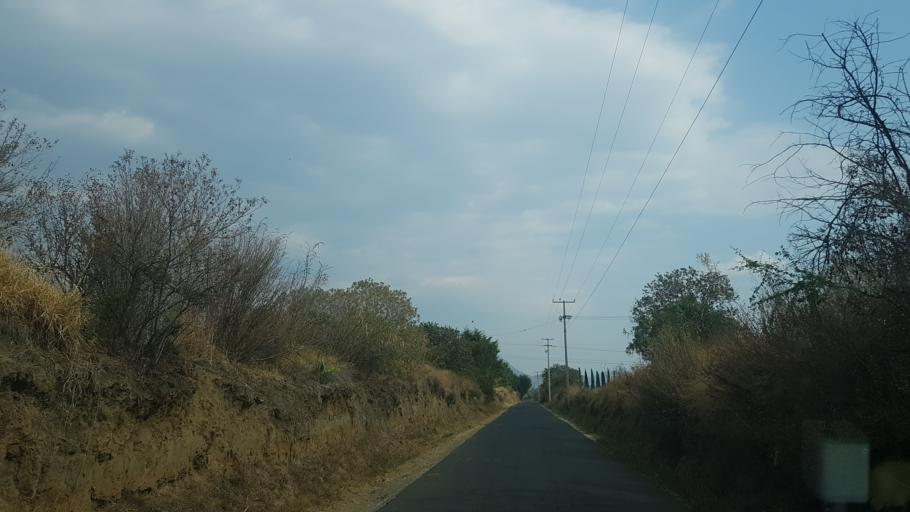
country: MX
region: Puebla
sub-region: Santa Isabel Cholula
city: Santa Ana Acozautla
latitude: 18.9549
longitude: -98.4005
